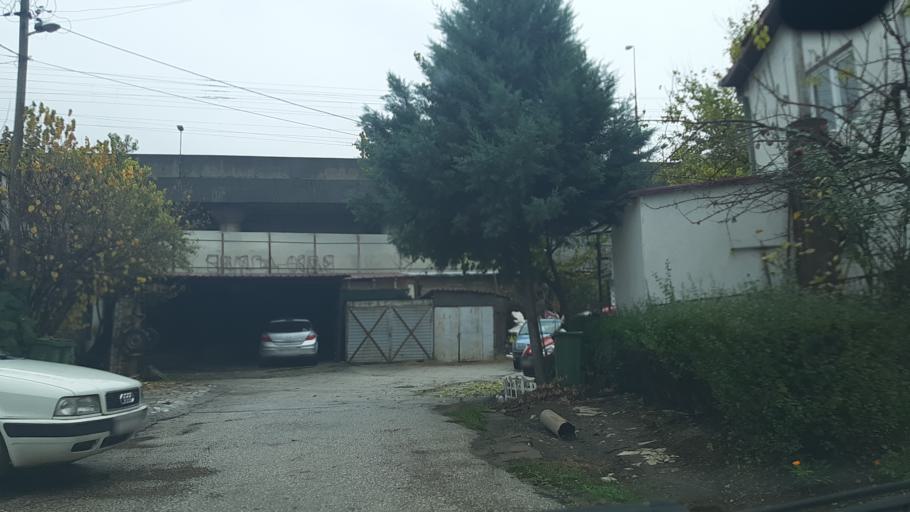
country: MK
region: Karpos
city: Skopje
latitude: 41.9941
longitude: 21.4483
